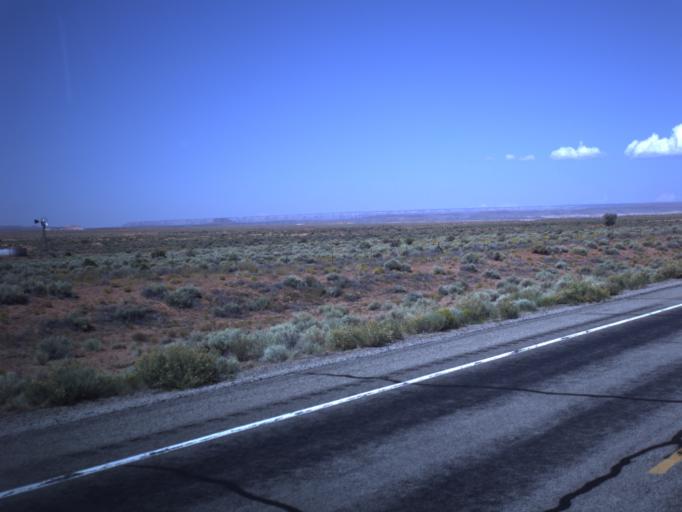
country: US
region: Utah
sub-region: San Juan County
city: Blanding
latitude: 37.1639
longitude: -109.5755
